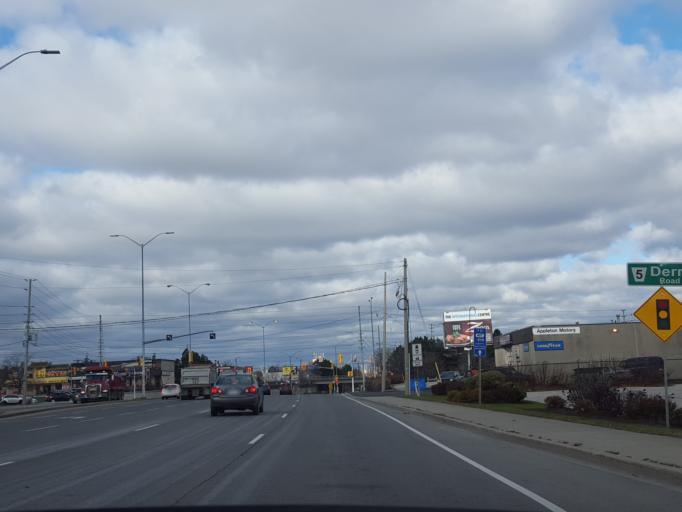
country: CA
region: Ontario
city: Etobicoke
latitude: 43.7027
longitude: -79.6409
